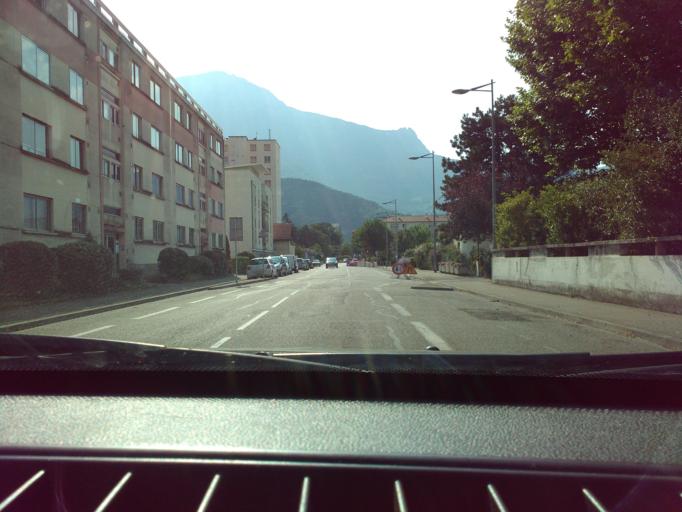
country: FR
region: Rhone-Alpes
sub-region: Departement de l'Isere
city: Grenoble
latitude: 45.1488
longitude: 5.7039
